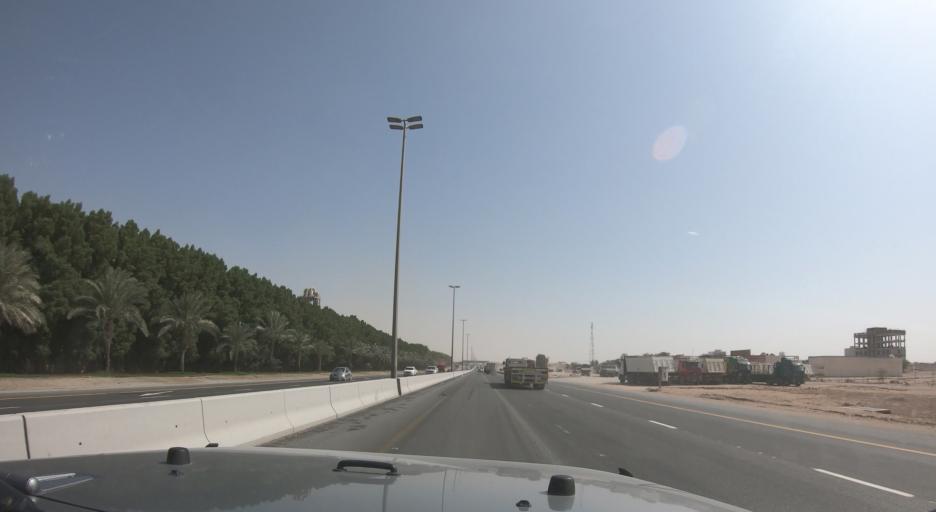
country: AE
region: Ash Shariqah
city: Sharjah
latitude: 25.2952
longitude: 55.6116
